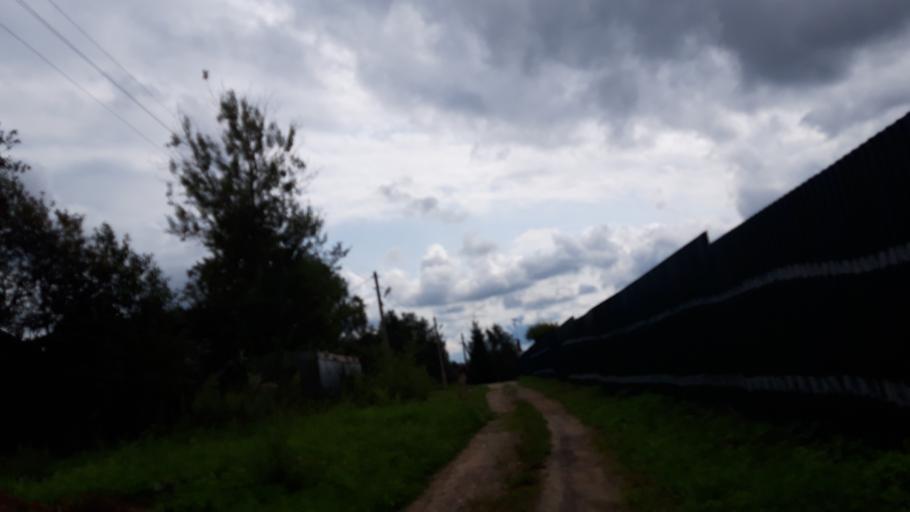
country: RU
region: Tverskaya
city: Konakovo
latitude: 56.6771
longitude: 36.7212
